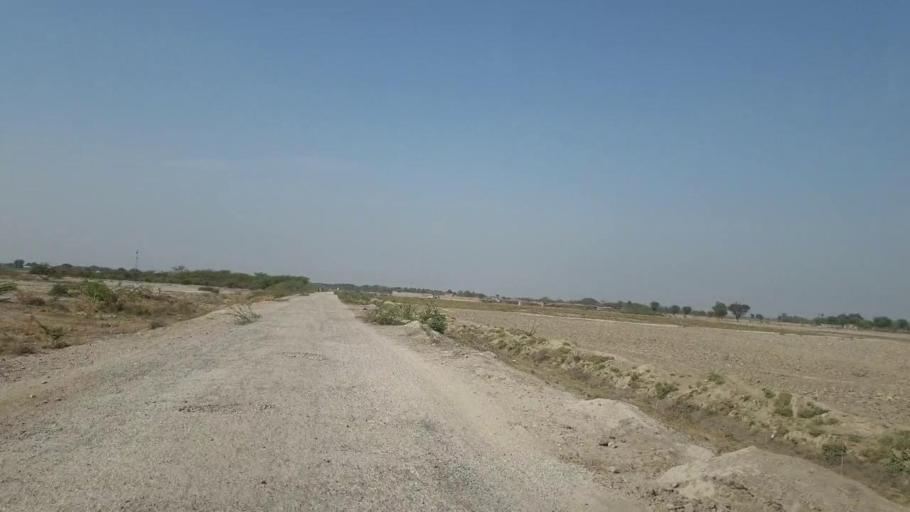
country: PK
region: Sindh
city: Nabisar
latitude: 25.0153
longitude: 69.5259
